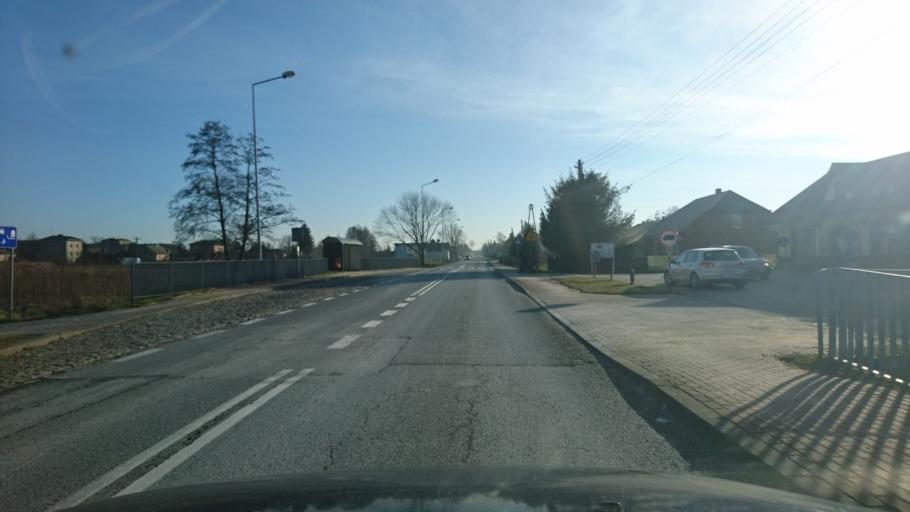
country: PL
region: Silesian Voivodeship
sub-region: Powiat klobucki
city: Starokrzepice
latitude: 51.0260
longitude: 18.6472
